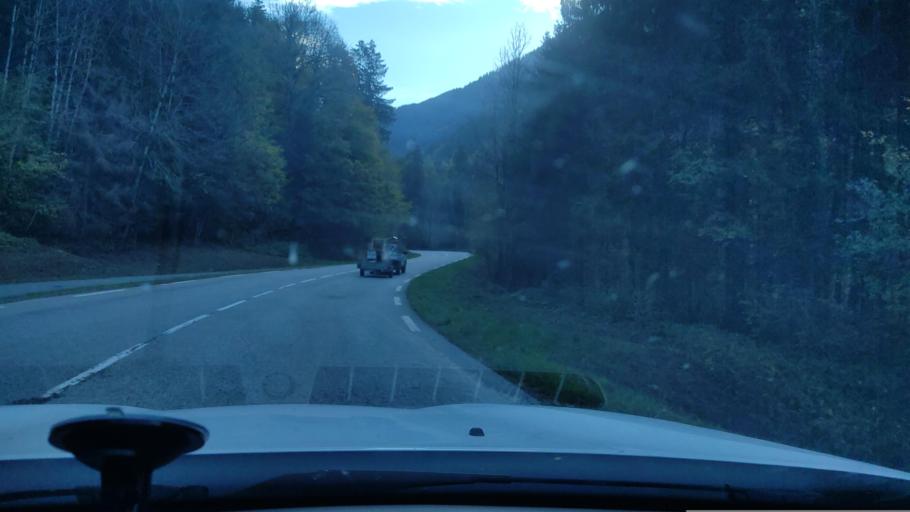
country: FR
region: Rhone-Alpes
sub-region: Departement de la Savoie
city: Marthod
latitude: 45.7175
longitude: 6.4887
